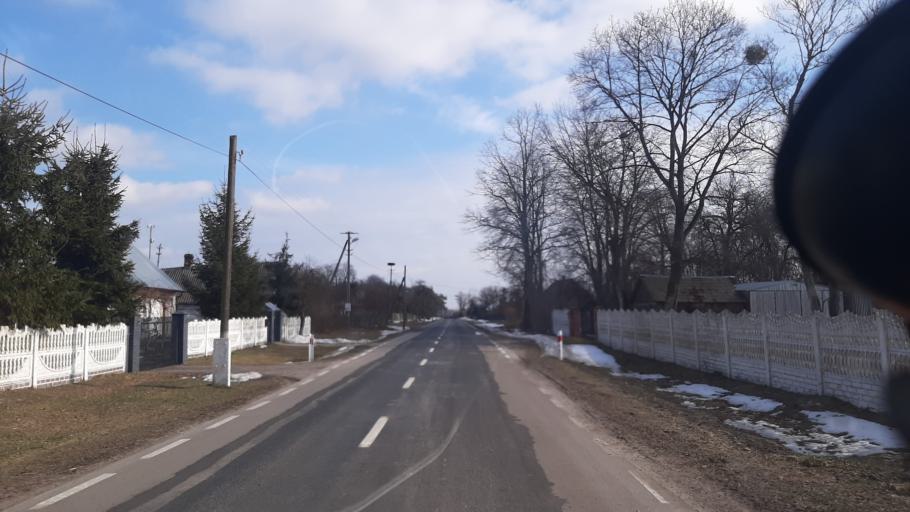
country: PL
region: Lublin Voivodeship
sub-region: Powiat wlodawski
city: Urszulin
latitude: 51.4959
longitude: 23.2153
